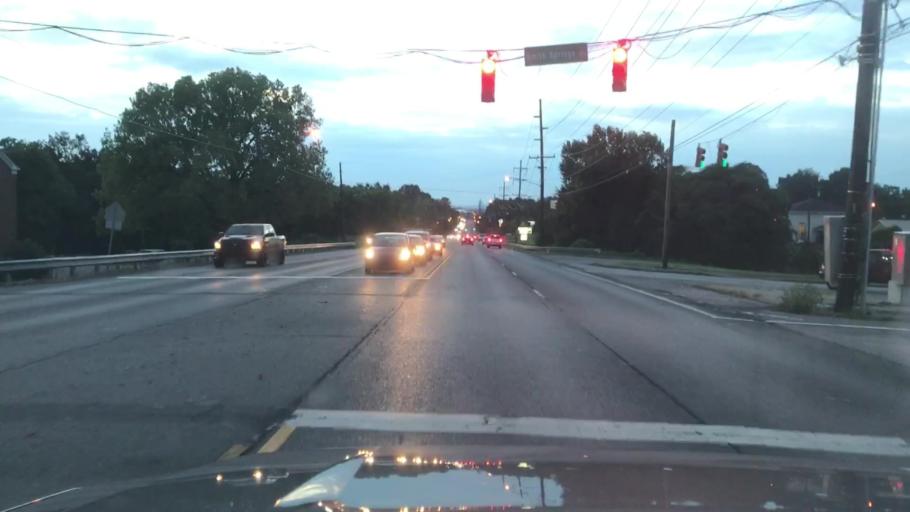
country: US
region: Tennessee
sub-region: Rutherford County
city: La Vergne
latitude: 36.0962
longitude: -86.6555
